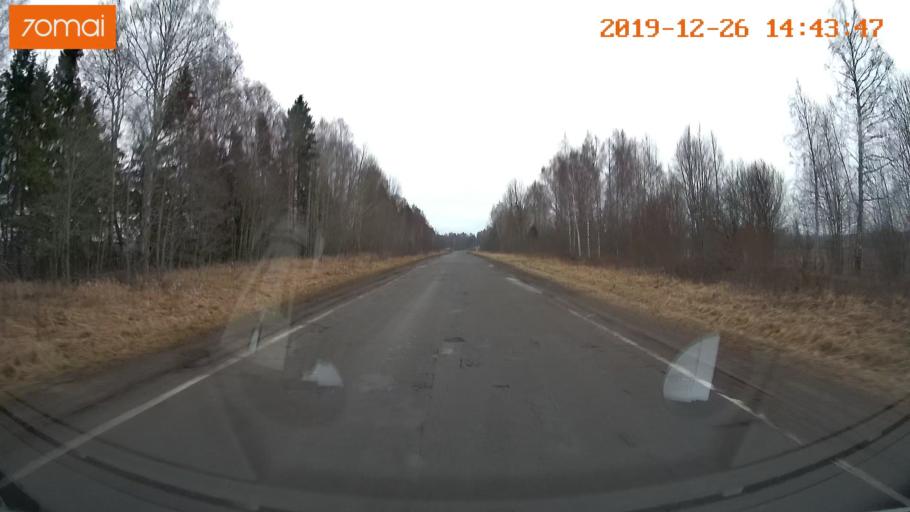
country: RU
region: Jaroslavl
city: Poshekhon'ye
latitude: 58.3535
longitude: 39.0443
